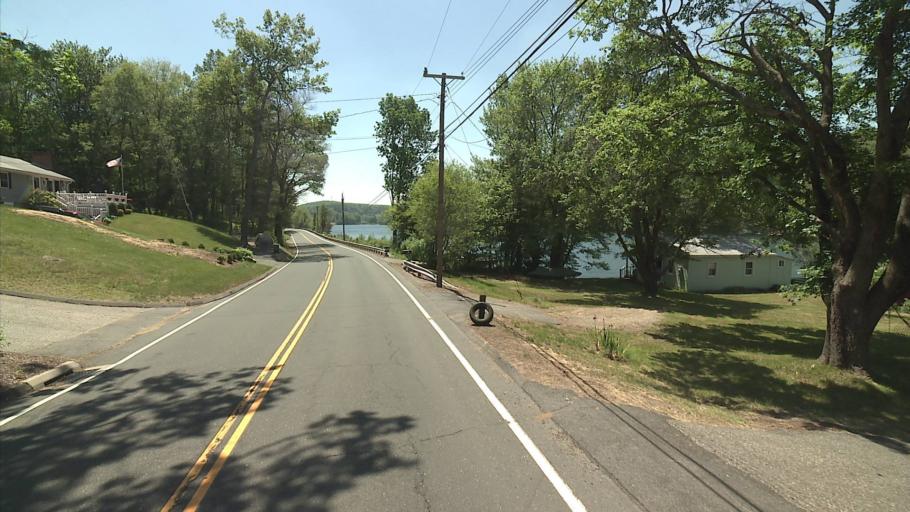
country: US
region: Connecticut
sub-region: Tolland County
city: Stafford
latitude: 42.0058
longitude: -72.2556
